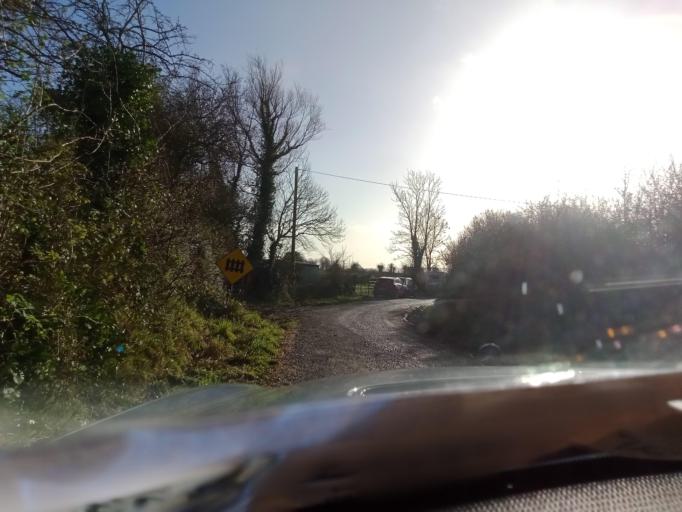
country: IE
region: Leinster
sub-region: Kilkenny
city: Mooncoin
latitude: 52.3154
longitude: -7.2808
